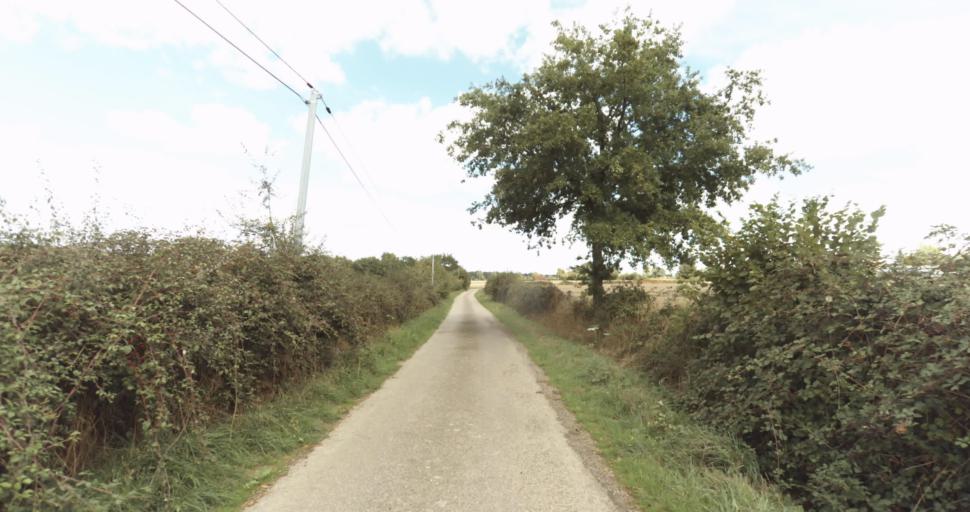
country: FR
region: Lower Normandy
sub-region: Departement du Calvados
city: Orbec
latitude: 48.9186
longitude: 0.3618
